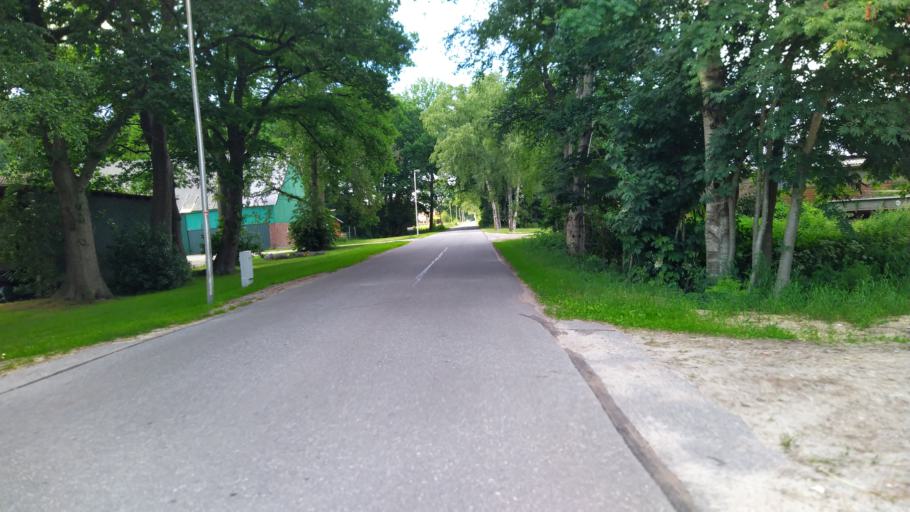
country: DE
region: Lower Saxony
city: Stinstedt
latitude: 53.6492
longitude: 8.9397
